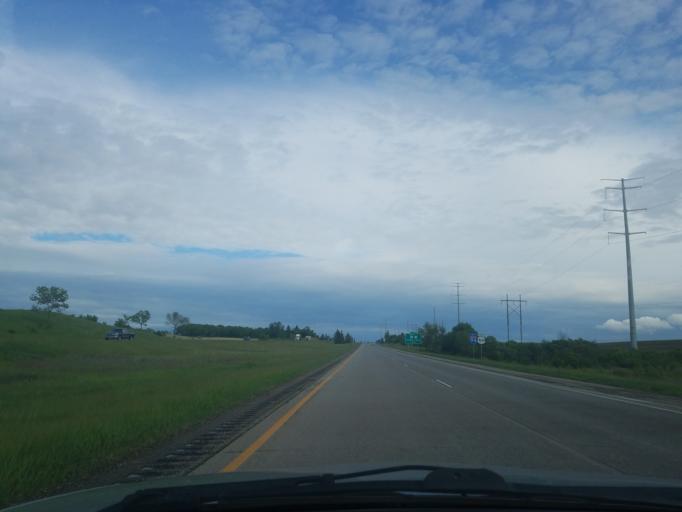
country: US
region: Minnesota
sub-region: Otter Tail County
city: Fergus Falls
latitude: 46.2212
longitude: -96.0356
